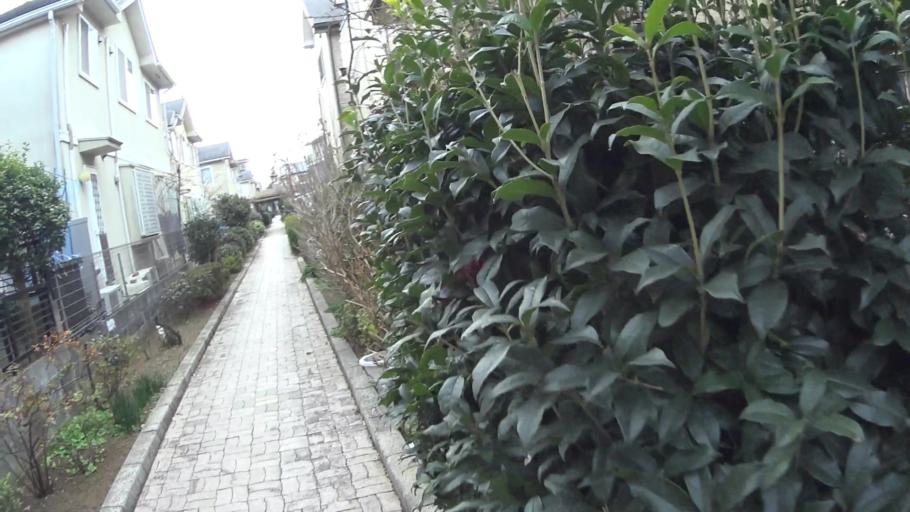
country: JP
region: Tokyo
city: Mitaka-shi
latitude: 35.6764
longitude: 139.5861
